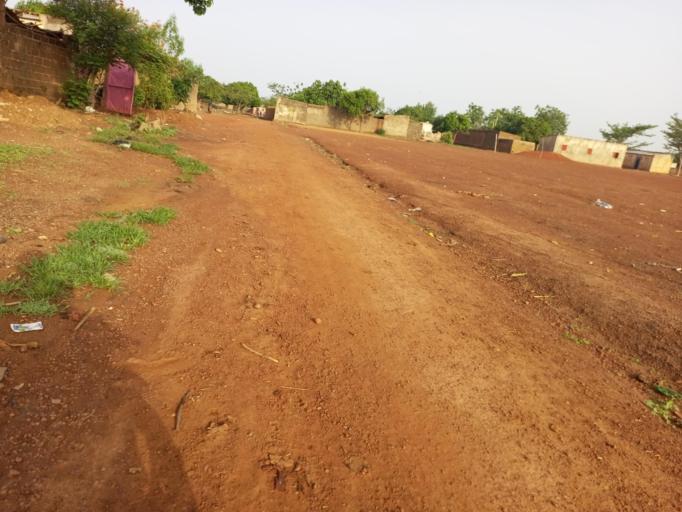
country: ML
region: Bamako
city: Bamako
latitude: 12.5184
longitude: -7.9887
